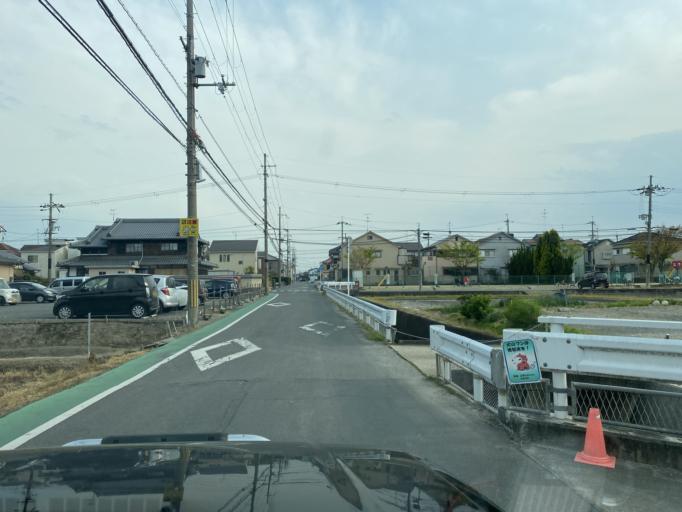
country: JP
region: Kyoto
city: Tanabe
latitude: 34.8144
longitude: 135.7824
